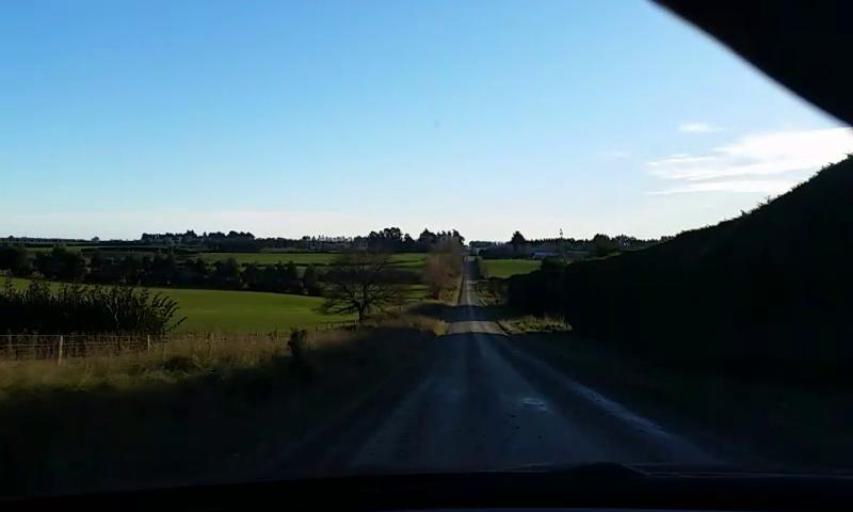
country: NZ
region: Southland
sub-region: Invercargill City
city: Invercargill
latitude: -46.2850
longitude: 168.5212
